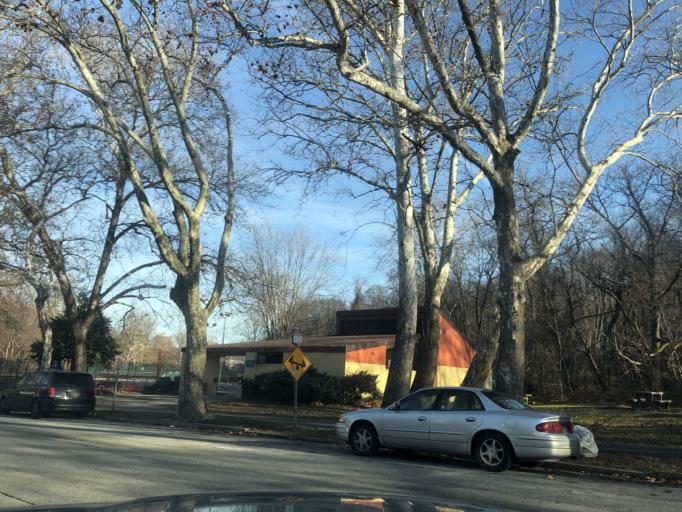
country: US
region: Pennsylvania
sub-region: Montgomery County
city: Bala-Cynwyd
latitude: 39.9820
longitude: -75.2265
